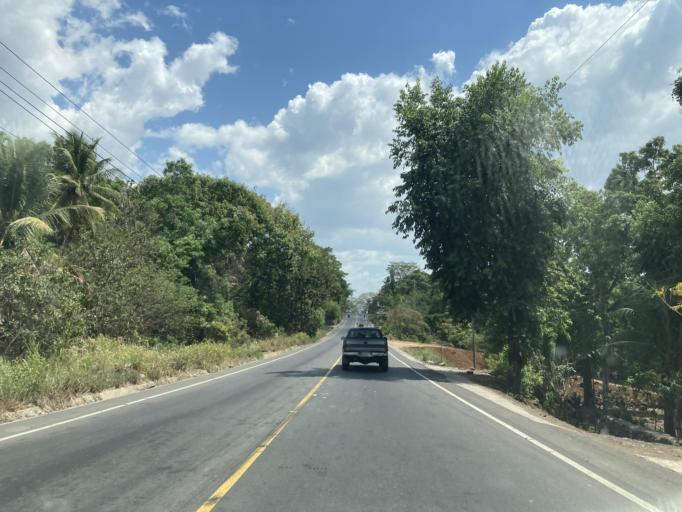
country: GT
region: Santa Rosa
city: Guazacapan
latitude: 14.0667
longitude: -90.4075
